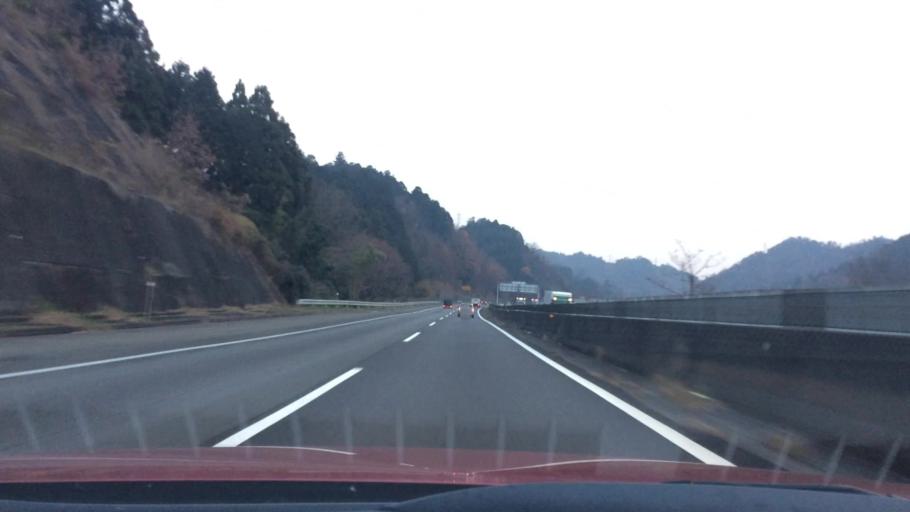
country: JP
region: Shiga Prefecture
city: Nagahama
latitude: 35.3108
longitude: 136.3136
